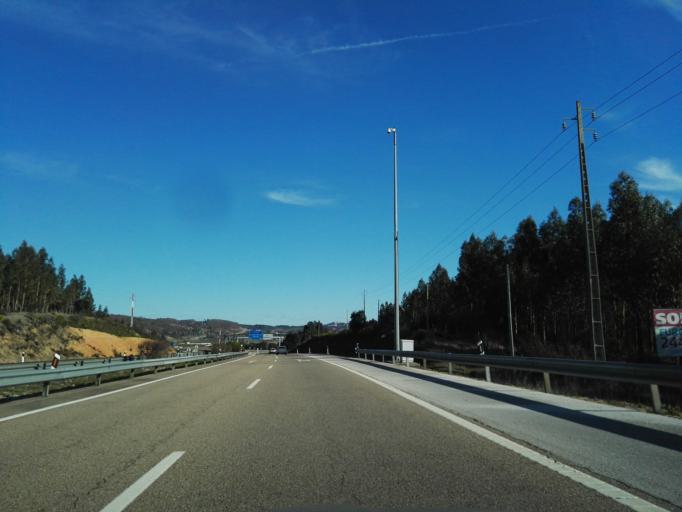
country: PT
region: Santarem
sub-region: Abrantes
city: Tramagal
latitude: 39.4866
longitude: -8.2817
